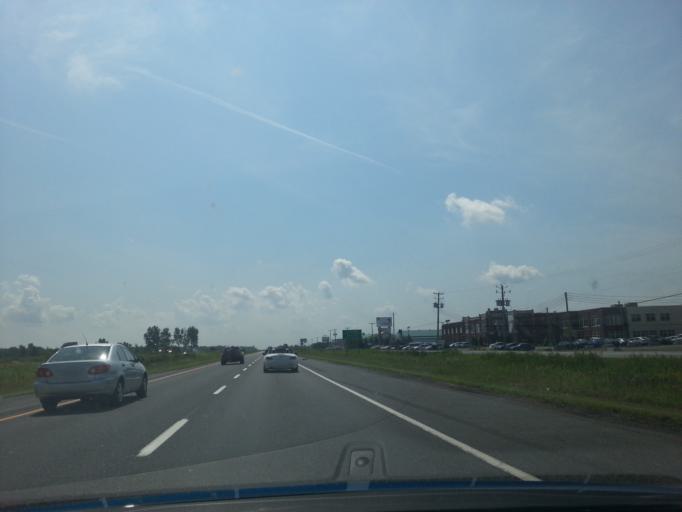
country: CA
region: Quebec
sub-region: Mauricie
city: Saint-Germain-de-Grantham
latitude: 45.8502
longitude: -72.5856
